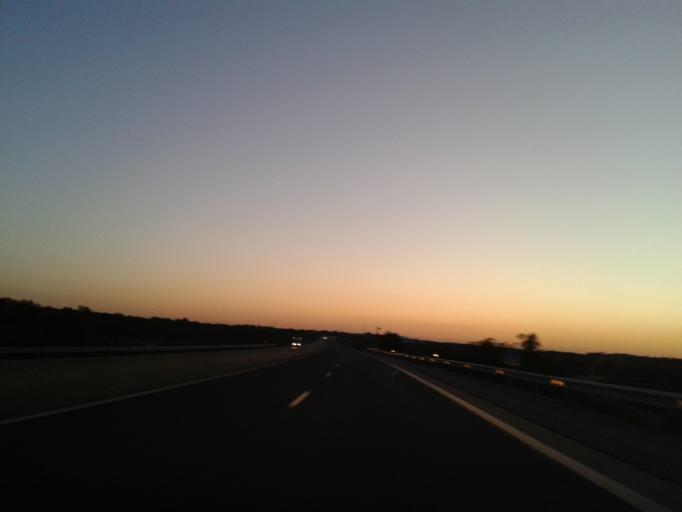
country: PT
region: Faro
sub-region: Albufeira
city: Guia
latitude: 37.1368
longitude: -8.2933
